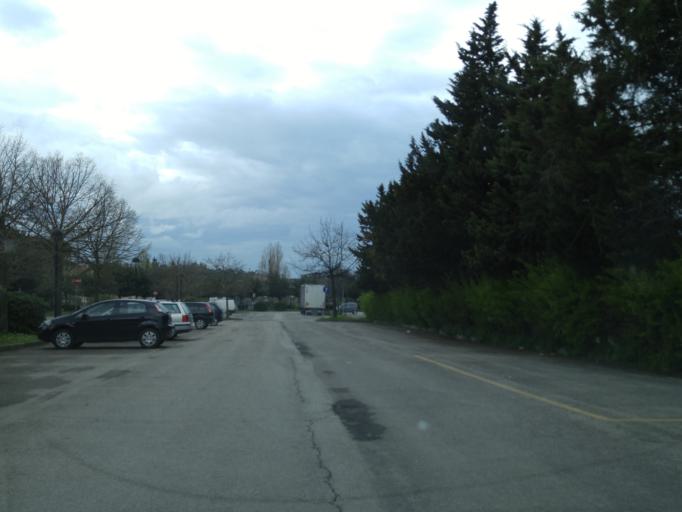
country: IT
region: The Marches
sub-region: Provincia di Pesaro e Urbino
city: Fano
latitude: 43.8433
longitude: 13.0085
